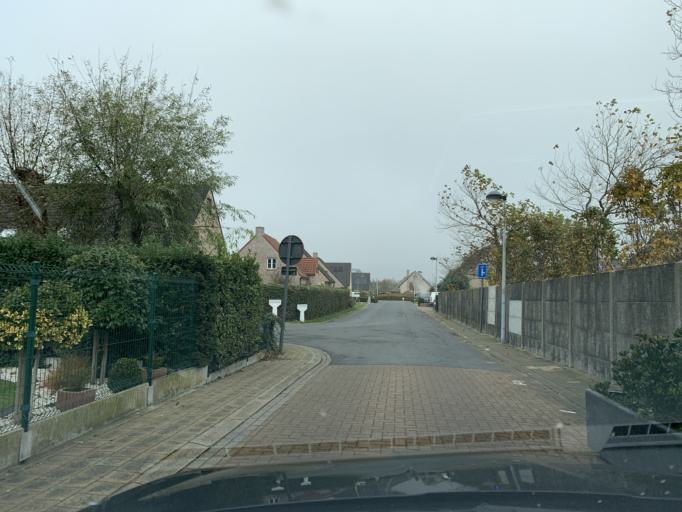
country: BE
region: Flanders
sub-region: Provincie West-Vlaanderen
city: De Panne
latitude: 51.0749
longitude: 2.5991
